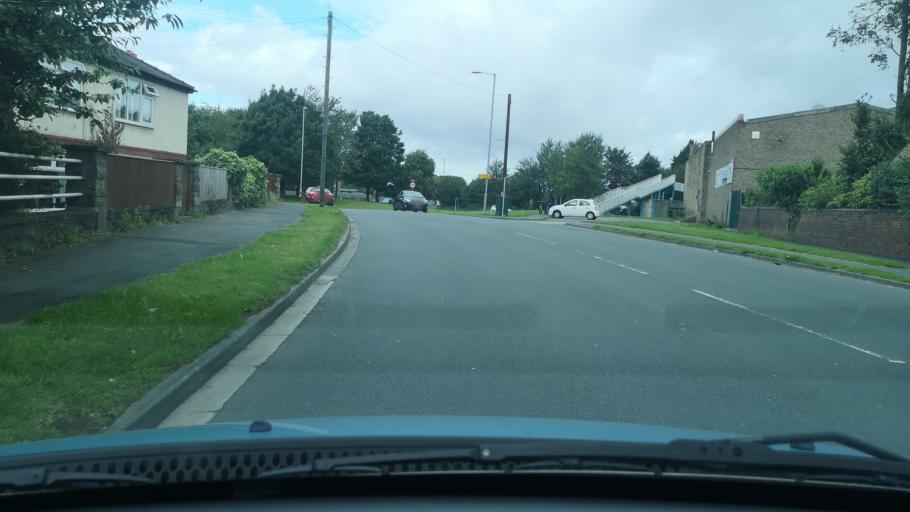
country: GB
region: England
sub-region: City and Borough of Wakefield
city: Ossett
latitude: 53.6923
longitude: -1.5904
